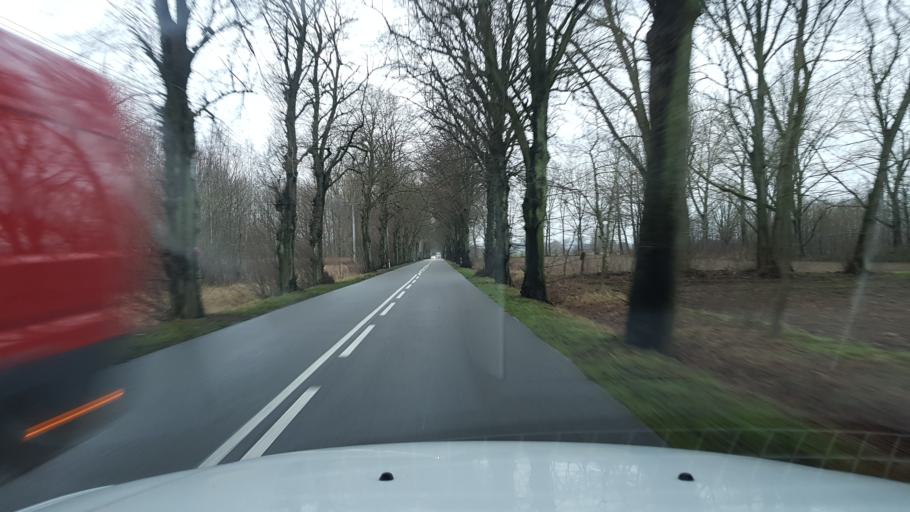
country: PL
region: West Pomeranian Voivodeship
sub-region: Powiat gryficki
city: Trzebiatow
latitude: 54.0589
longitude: 15.3211
